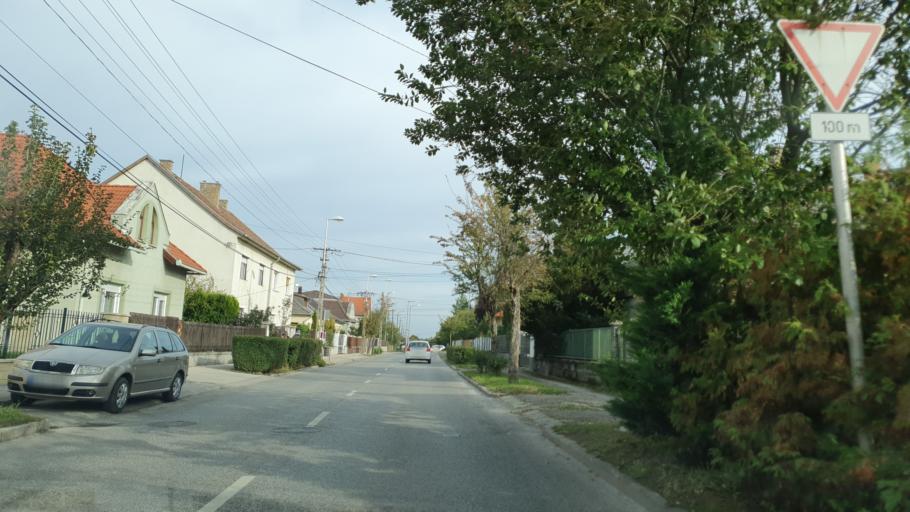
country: HU
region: Veszprem
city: Veszprem
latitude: 47.0933
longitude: 17.9241
